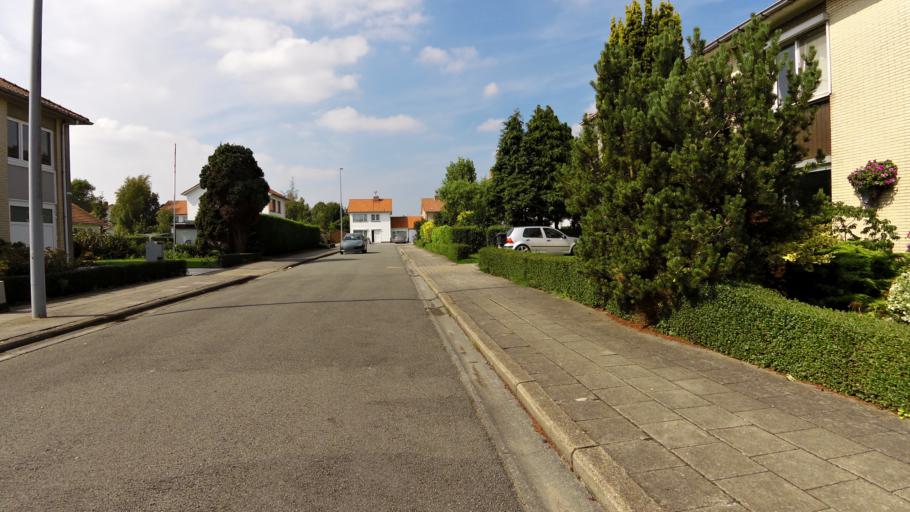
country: BE
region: Flanders
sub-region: Provincie West-Vlaanderen
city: Ostend
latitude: 51.1774
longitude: 2.8809
